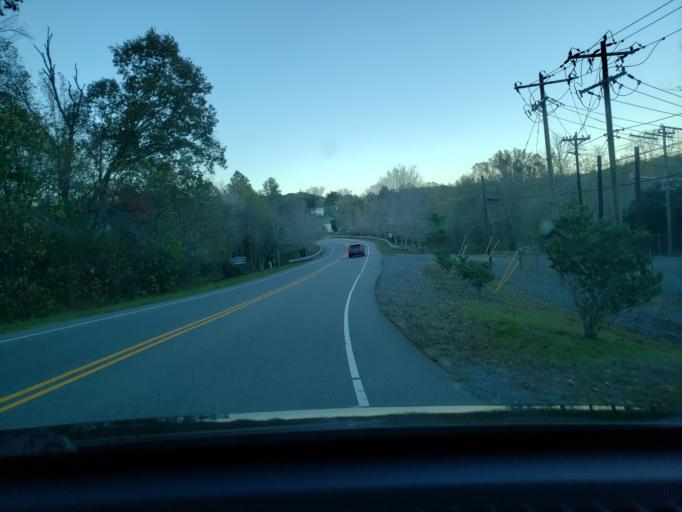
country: US
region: North Carolina
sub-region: Stokes County
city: Danbury
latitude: 36.4058
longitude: -80.2020
